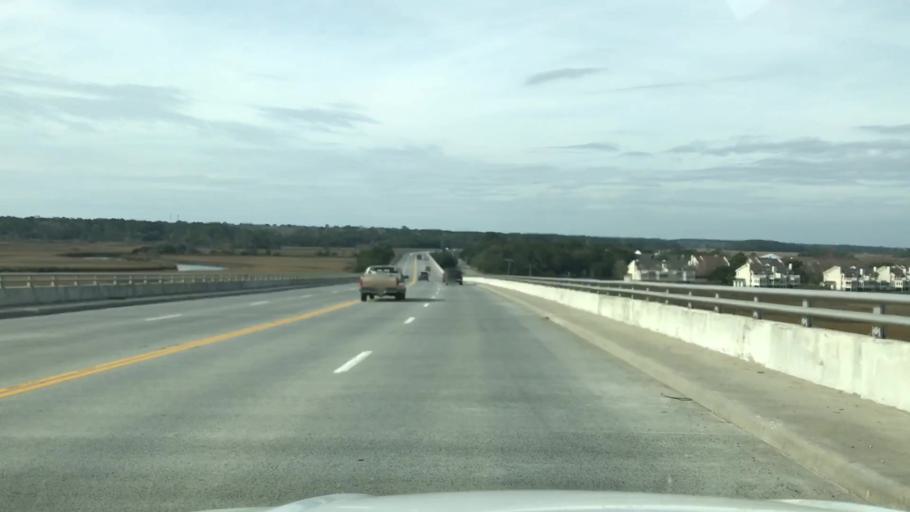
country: US
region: South Carolina
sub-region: Charleston County
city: Charleston
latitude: 32.7526
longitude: -80.0130
